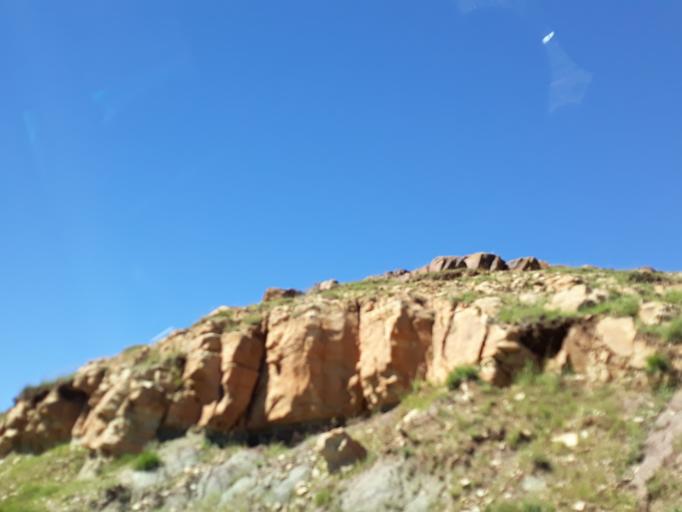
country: LS
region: Mohale's Hoek District
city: Mohale's Hoek
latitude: -30.1047
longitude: 27.4834
